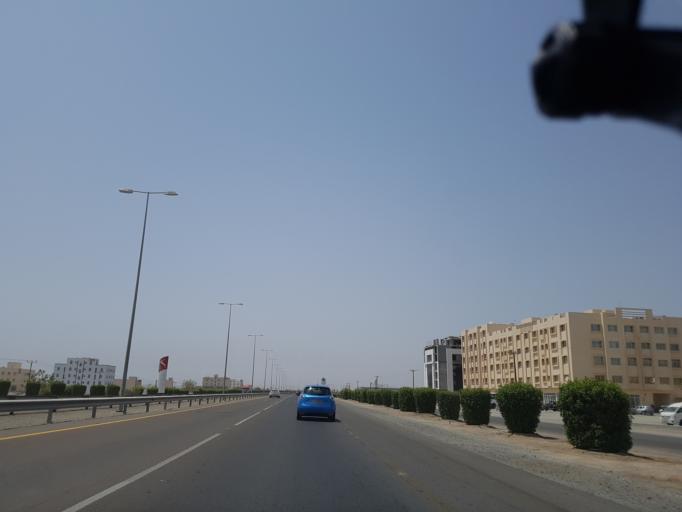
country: OM
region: Al Batinah
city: Al Liwa'
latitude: 24.4170
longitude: 56.6034
